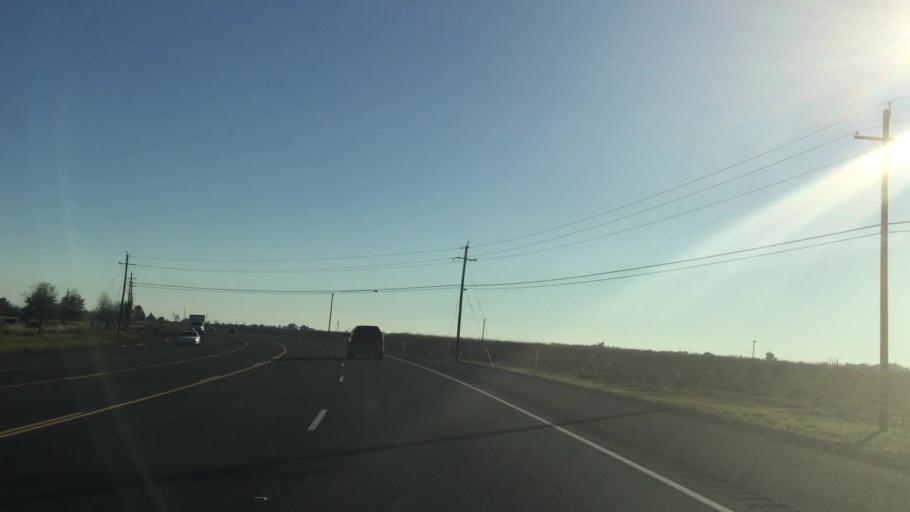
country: US
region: California
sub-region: Butte County
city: Gridley
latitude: 39.3786
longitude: -121.6131
